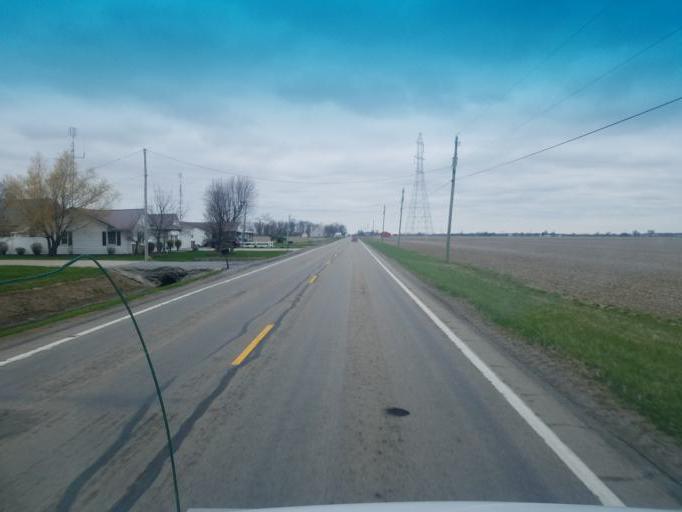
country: US
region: Ohio
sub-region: Allen County
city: Delphos
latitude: 40.8966
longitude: -84.3505
